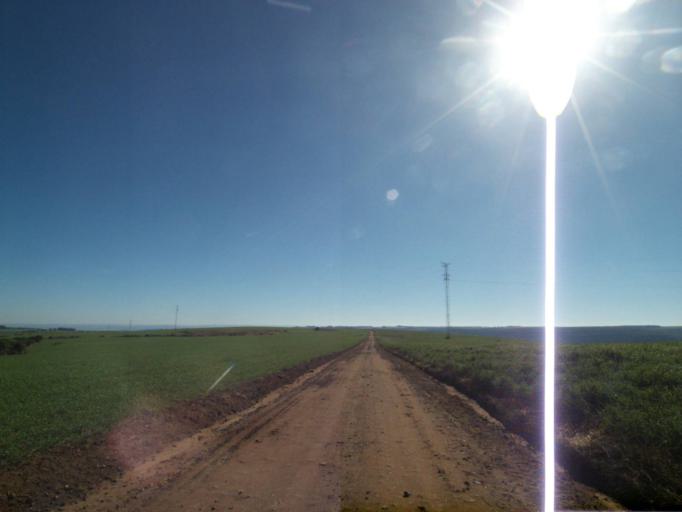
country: BR
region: Parana
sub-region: Tibagi
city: Tibagi
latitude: -24.5801
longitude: -50.2658
